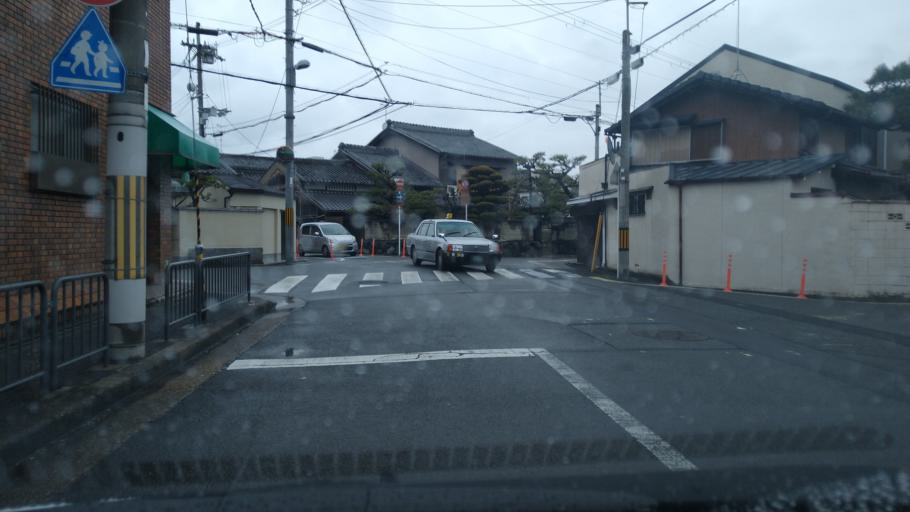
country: JP
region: Kyoto
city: Muko
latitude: 34.9747
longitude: 135.7307
